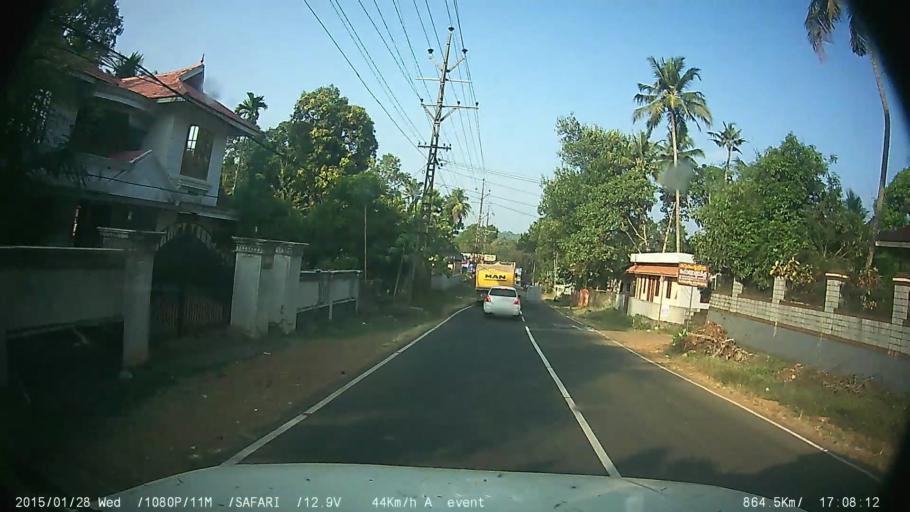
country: IN
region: Kerala
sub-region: Kottayam
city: Changanacheri
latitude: 9.4815
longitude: 76.5735
